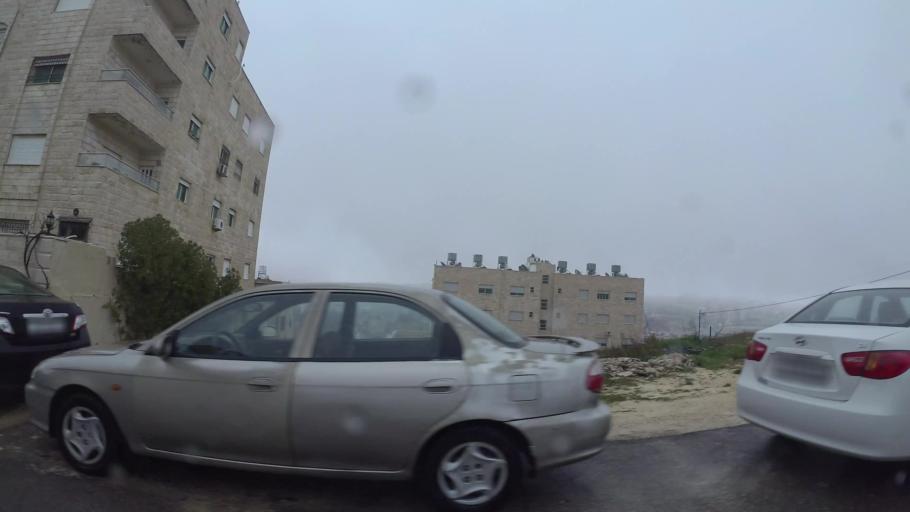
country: JO
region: Amman
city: Al Jubayhah
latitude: 32.0162
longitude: 35.8409
